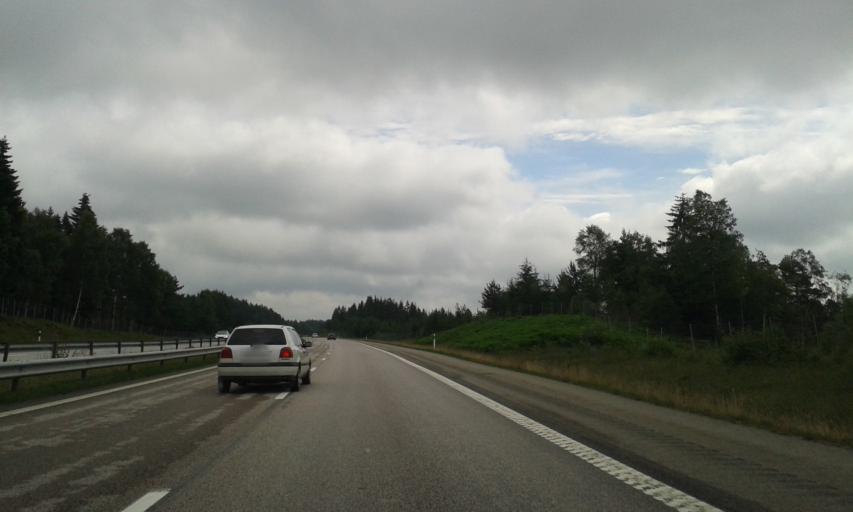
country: SE
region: Vaestra Goetaland
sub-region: Bollebygds Kommun
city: Bollebygd
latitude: 57.6720
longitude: 12.6684
